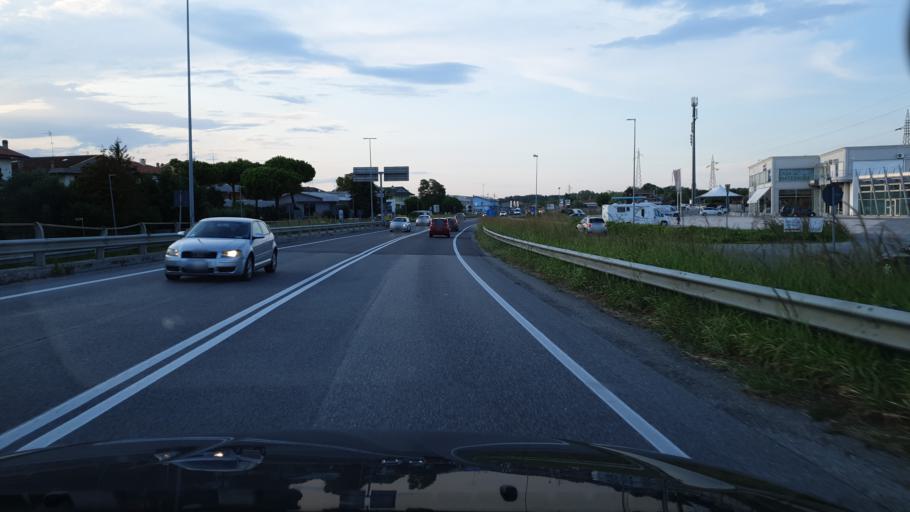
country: IT
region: Emilia-Romagna
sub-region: Forli-Cesena
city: Cesenatico
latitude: 44.1987
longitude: 12.3898
